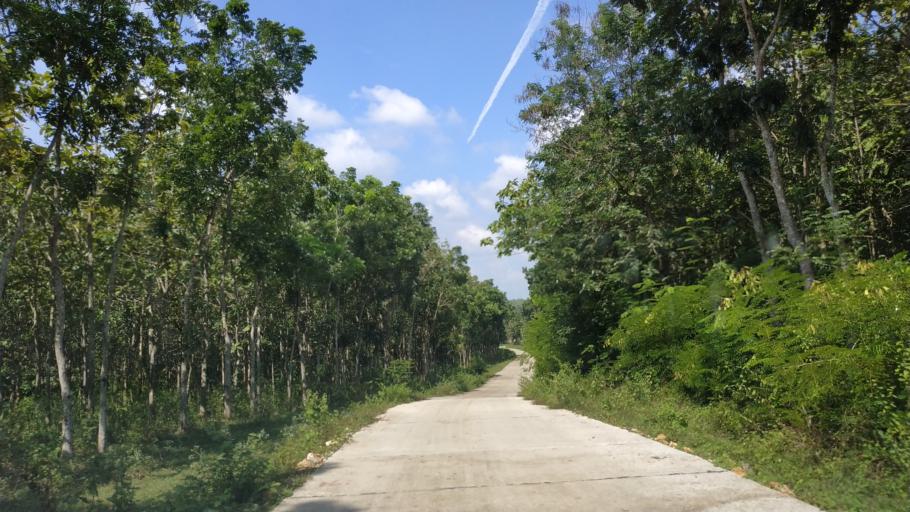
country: ID
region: Central Java
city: Guyangan
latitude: -7.0023
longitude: 111.0879
